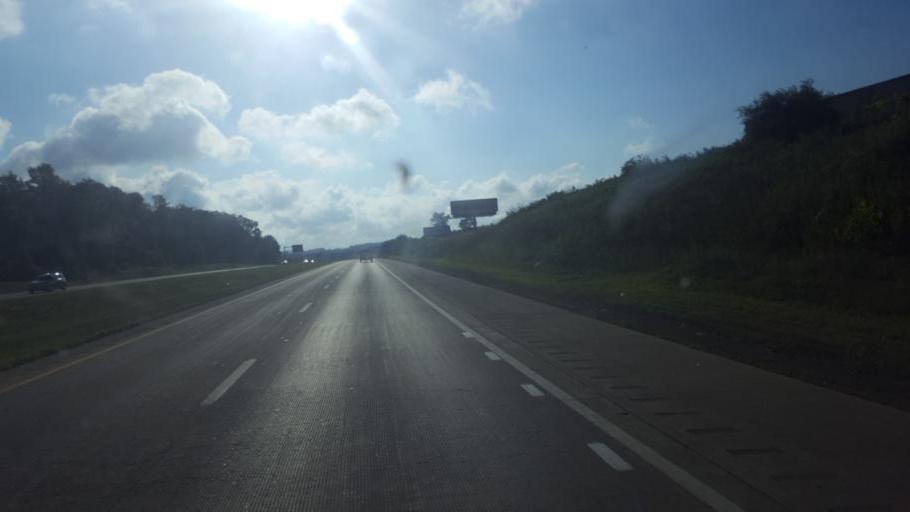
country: US
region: Ohio
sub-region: Wayne County
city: Wooster
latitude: 40.7990
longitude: -81.9026
